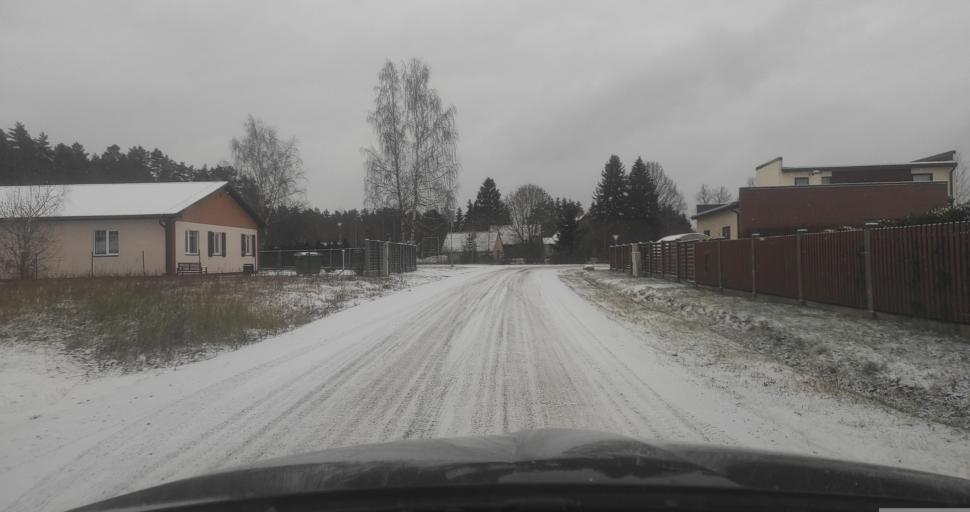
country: LV
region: Babite
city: Pinki
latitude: 56.9059
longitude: 23.8334
